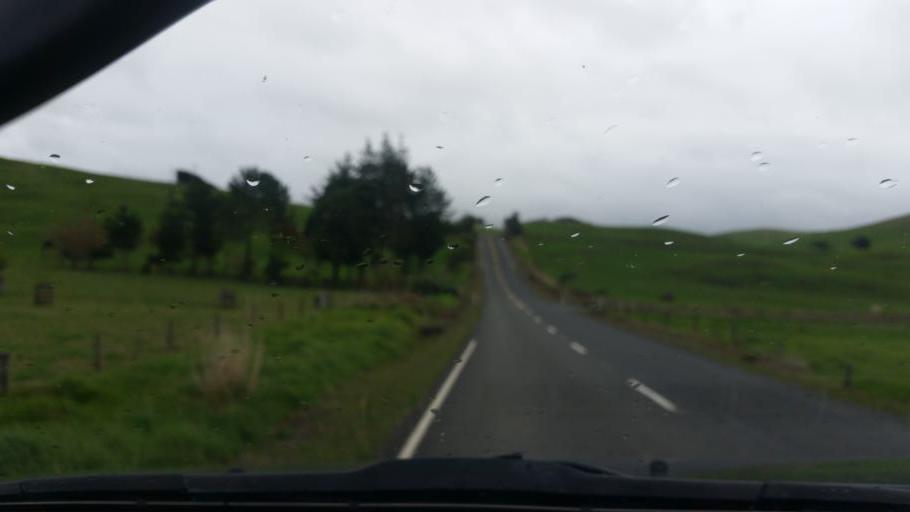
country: NZ
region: Northland
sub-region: Kaipara District
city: Dargaville
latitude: -36.0225
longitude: 173.9864
